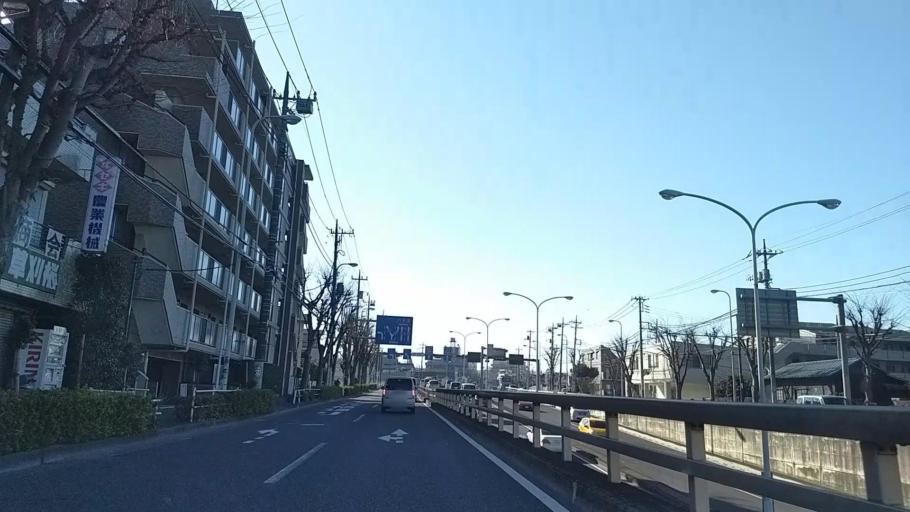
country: JP
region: Tokyo
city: Hino
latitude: 35.6507
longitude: 139.4375
